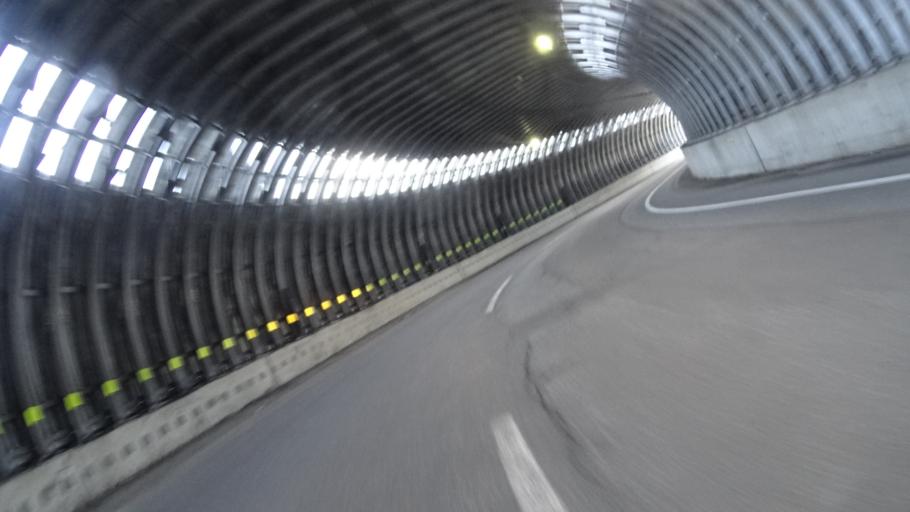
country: JP
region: Niigata
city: Shiozawa
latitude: 36.9846
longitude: 138.7819
